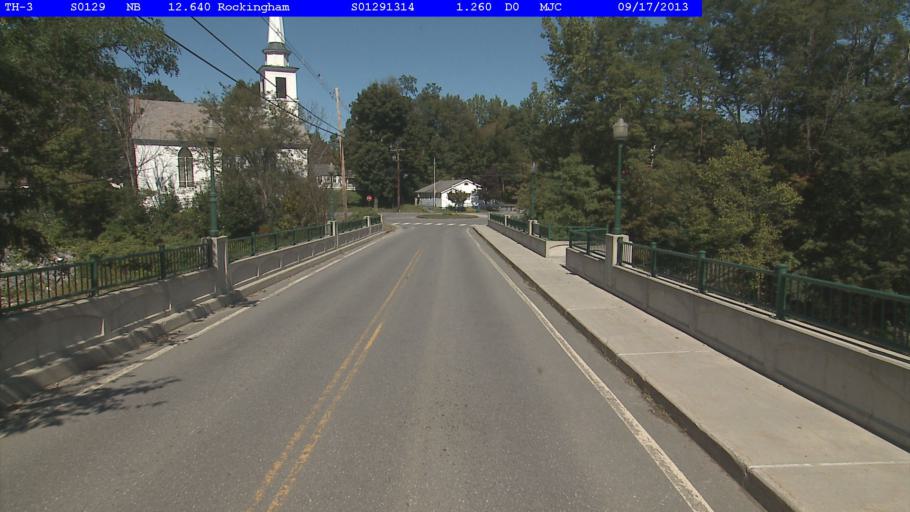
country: US
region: Vermont
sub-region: Windham County
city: Rockingham
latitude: 43.1376
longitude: -72.5099
